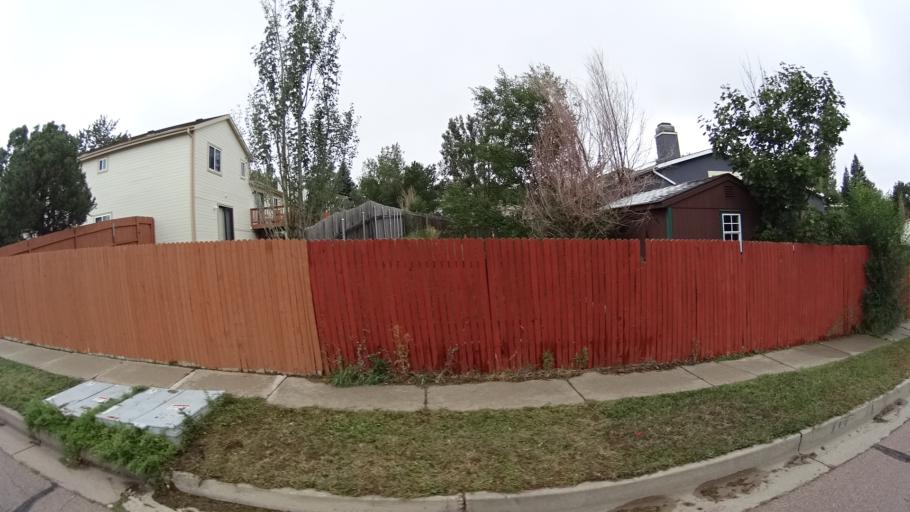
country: US
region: Colorado
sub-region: El Paso County
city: Cimarron Hills
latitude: 38.9204
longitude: -104.7608
